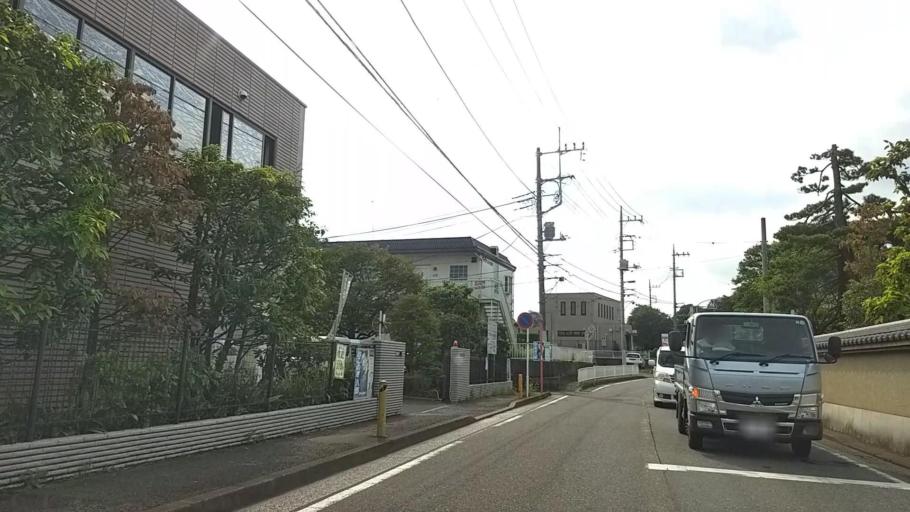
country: JP
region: Kanagawa
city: Yokohama
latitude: 35.4918
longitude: 139.5884
